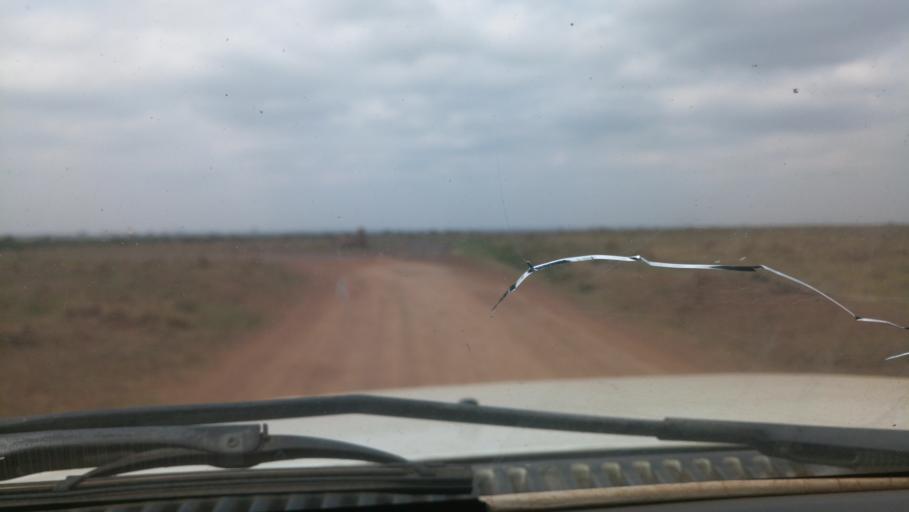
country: KE
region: Nairobi Area
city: Nairobi
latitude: -1.3516
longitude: 36.7983
